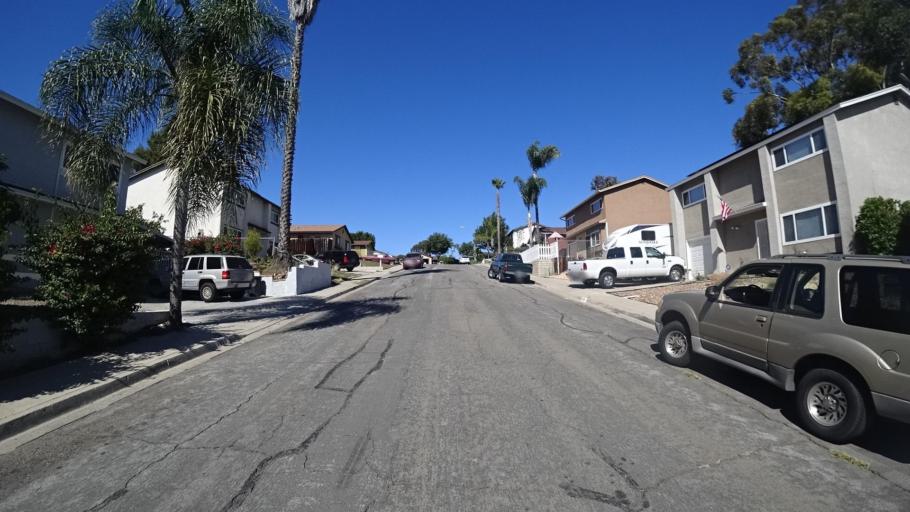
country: US
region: California
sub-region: San Diego County
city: Lemon Grove
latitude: 32.7173
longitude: -117.0235
